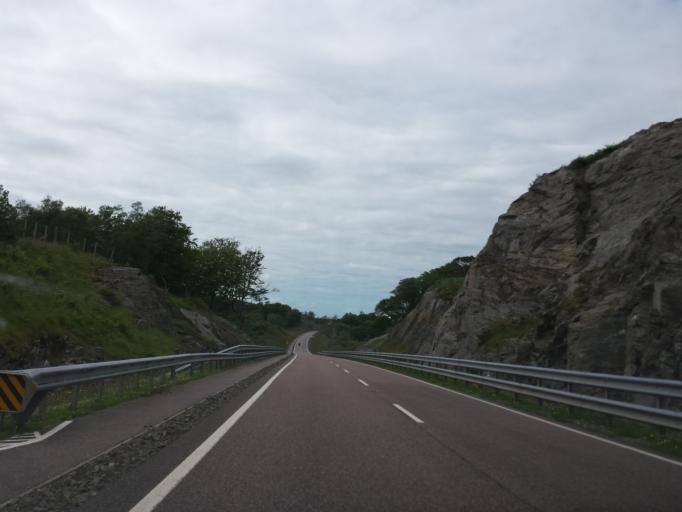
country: GB
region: Scotland
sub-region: Argyll and Bute
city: Isle Of Mull
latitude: 56.9021
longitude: -5.8079
